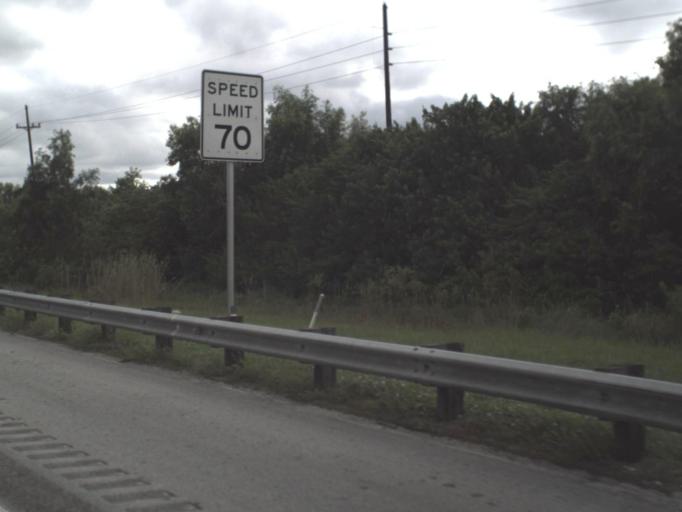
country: US
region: Florida
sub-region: Palm Beach County
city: Limestone Creek
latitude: 26.9296
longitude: -80.1516
